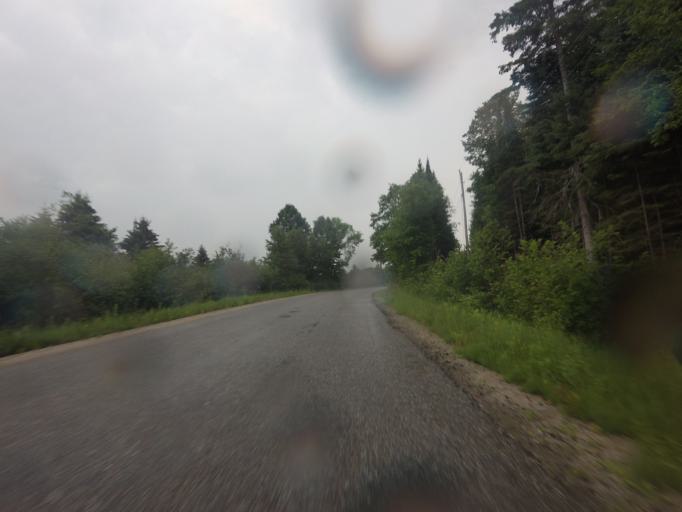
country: CA
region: Quebec
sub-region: Outaouais
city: Maniwaki
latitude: 46.4276
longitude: -75.9511
